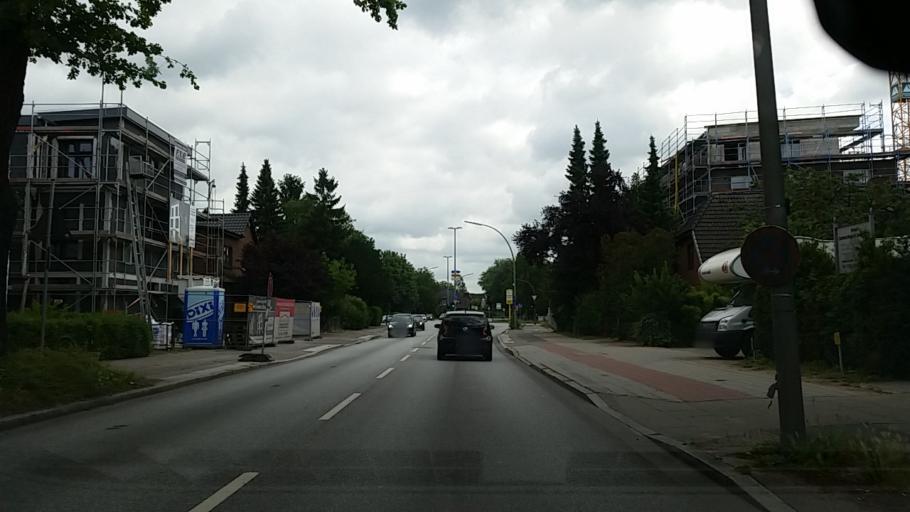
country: DE
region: Schleswig-Holstein
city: Bonningstedt
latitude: 53.6367
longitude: 9.9185
